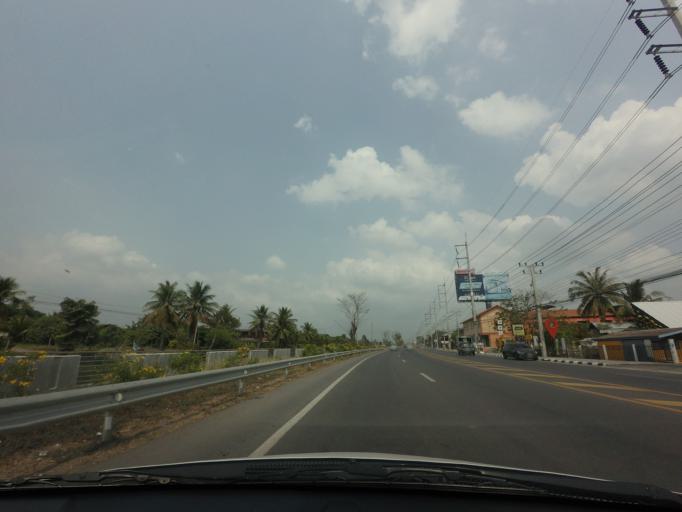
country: TH
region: Pathum Thani
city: Thanyaburi
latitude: 14.0500
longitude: 100.7100
